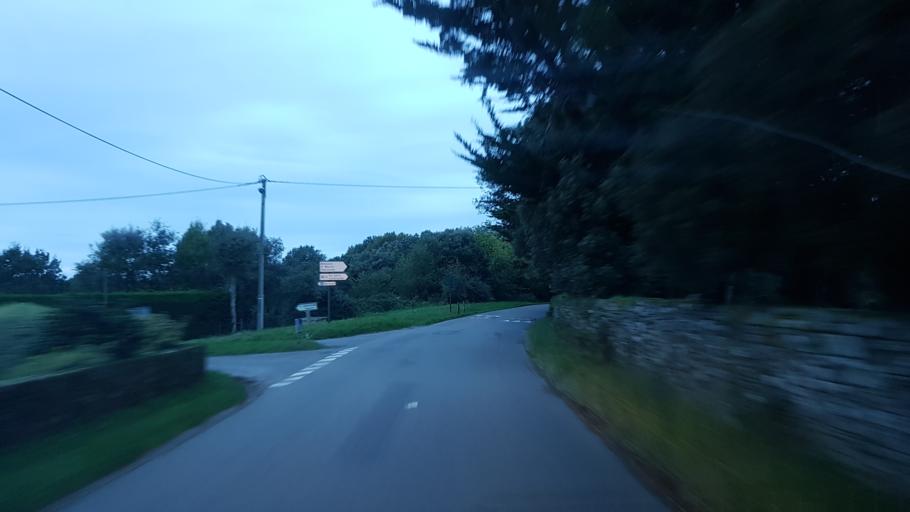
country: FR
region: Brittany
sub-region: Departement du Morbihan
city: Sarzeau
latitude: 47.5369
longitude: -2.7793
